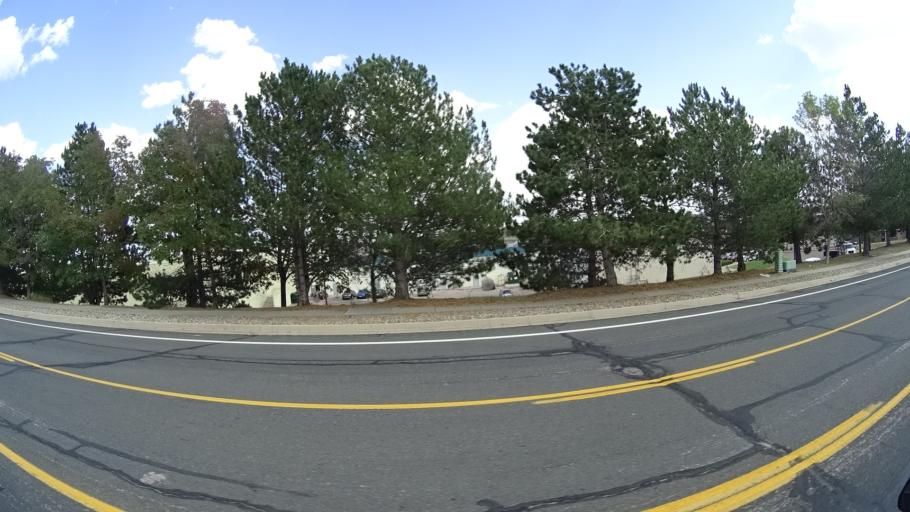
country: US
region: Colorado
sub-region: El Paso County
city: Cimarron Hills
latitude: 38.8733
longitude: -104.7233
